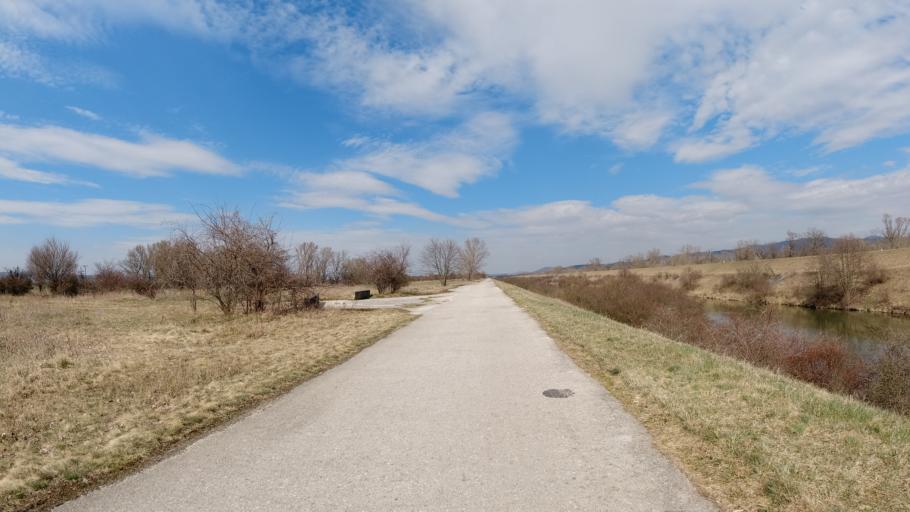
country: SK
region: Trnavsky
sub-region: Okres Trnava
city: Piestany
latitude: 48.6300
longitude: 17.8417
